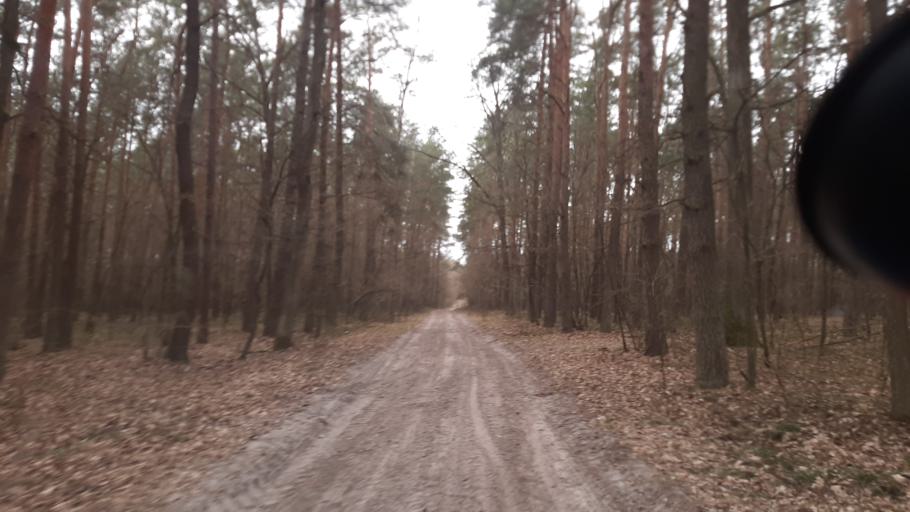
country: PL
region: Lublin Voivodeship
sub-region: Powiat lubelski
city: Garbow
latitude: 51.3998
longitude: 22.3713
